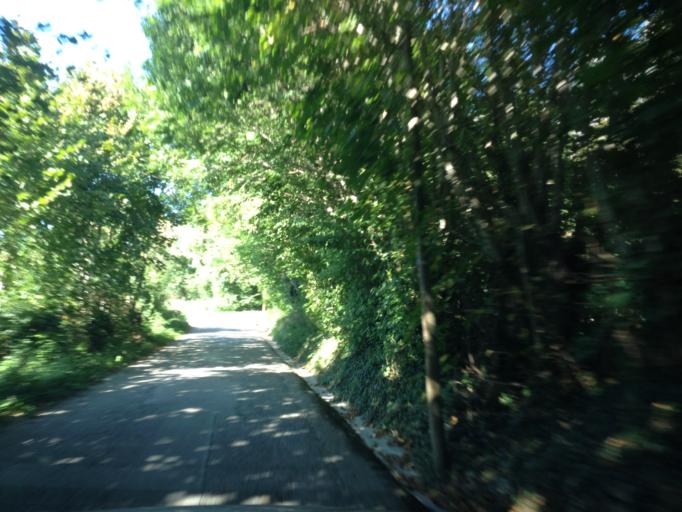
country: FR
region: Rhone-Alpes
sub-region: Departement de la Savoie
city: Mery
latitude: 45.6450
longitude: 5.9389
